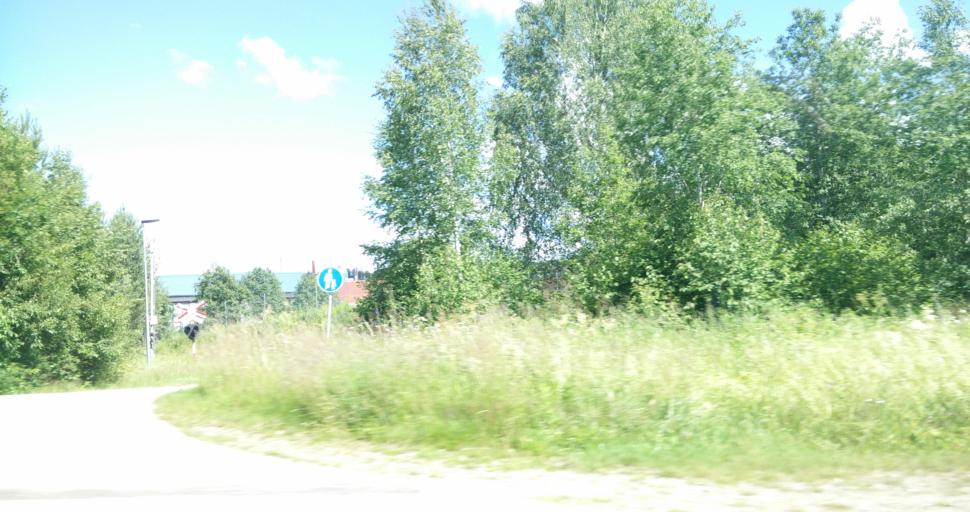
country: SE
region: Vaermland
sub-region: Hagfors Kommun
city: Hagfors
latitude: 60.0259
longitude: 13.6789
